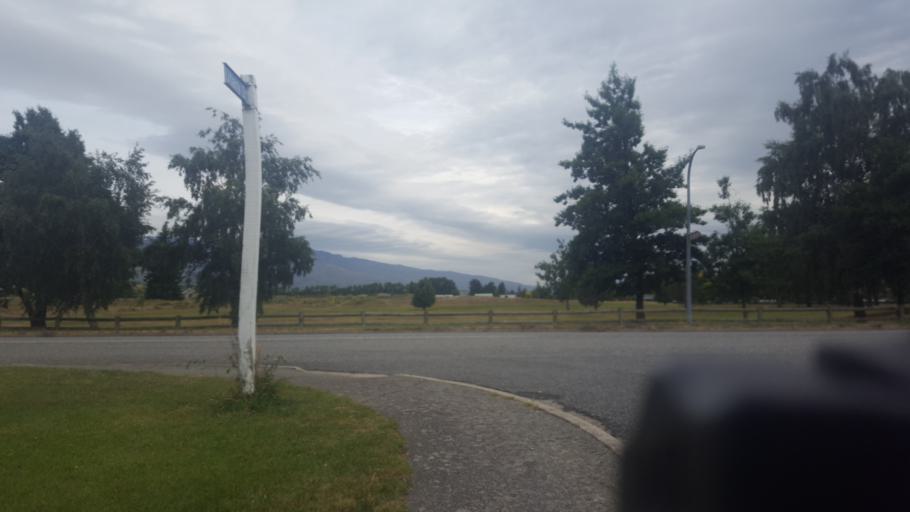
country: NZ
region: Otago
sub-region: Queenstown-Lakes District
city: Wanaka
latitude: -45.0419
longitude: 169.2106
